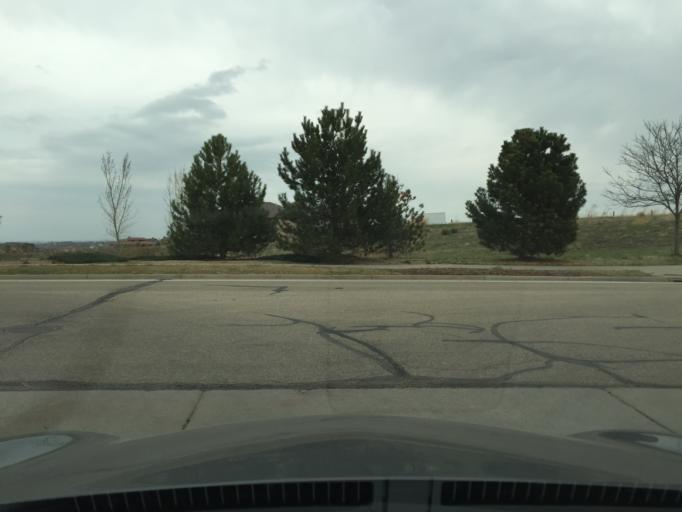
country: US
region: Colorado
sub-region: Boulder County
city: Erie
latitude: 40.0044
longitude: -105.0338
